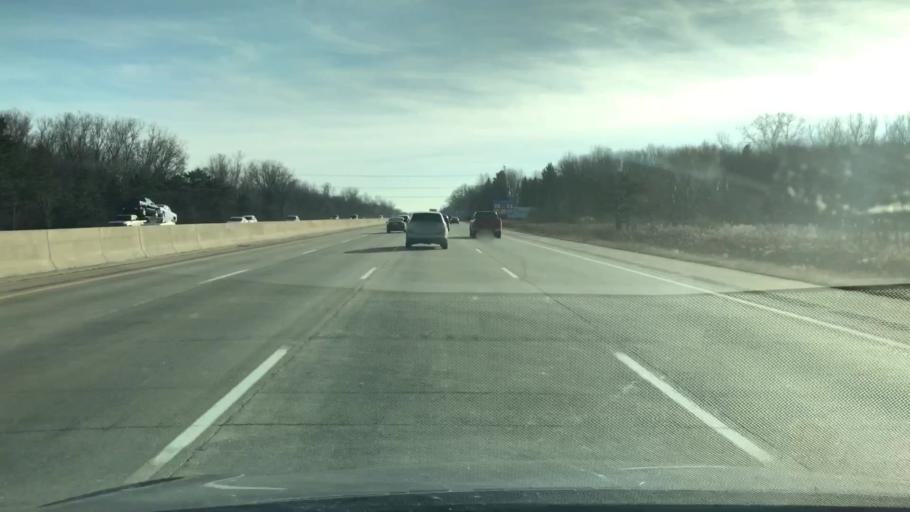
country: US
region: Michigan
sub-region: Genesee County
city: Clio
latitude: 43.2035
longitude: -83.7693
